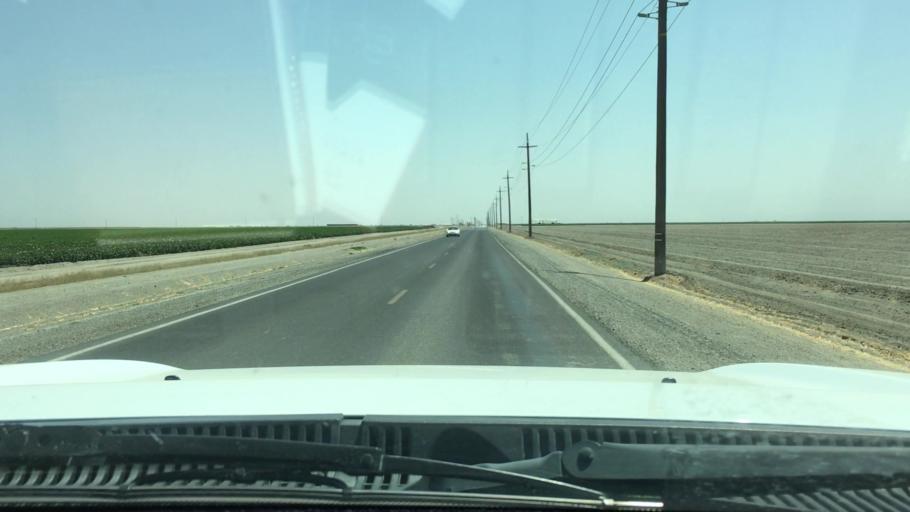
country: US
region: California
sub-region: Kings County
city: Corcoran
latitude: 36.0045
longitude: -119.5721
